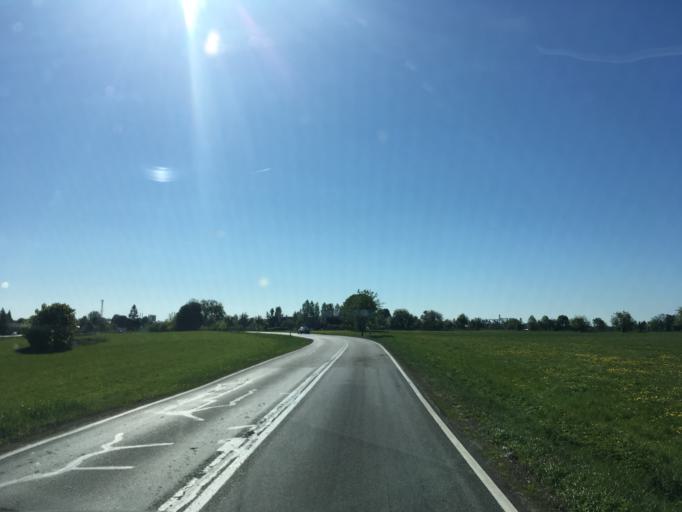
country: PL
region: Warmian-Masurian Voivodeship
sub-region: Powiat szczycienski
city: Szczytno
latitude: 53.5689
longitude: 20.9522
